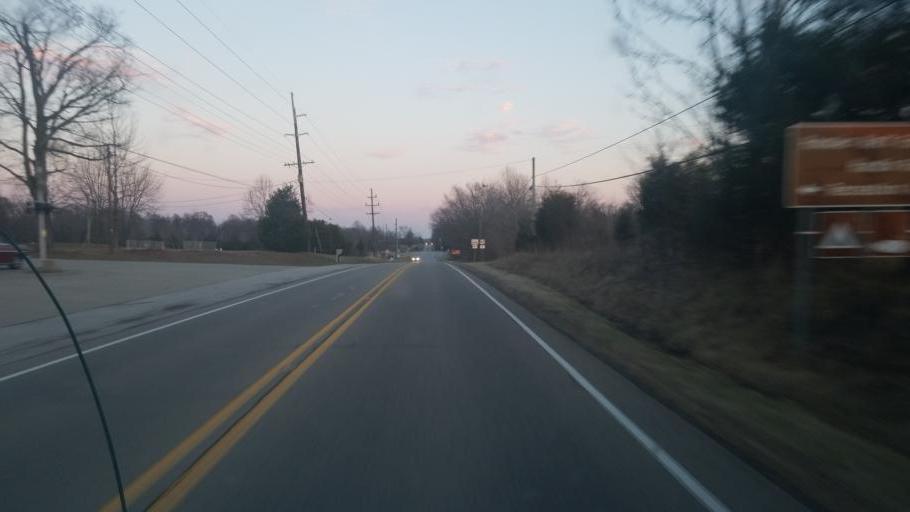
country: US
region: Indiana
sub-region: Lawrence County
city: Bedford
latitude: 38.8747
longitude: -86.3445
